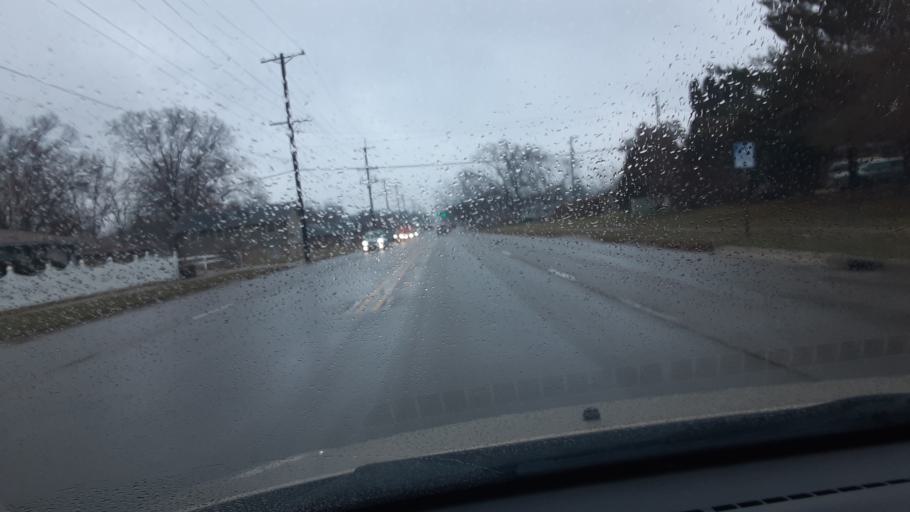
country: US
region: Illinois
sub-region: Winnebago County
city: Rockford
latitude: 42.3084
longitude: -89.0969
